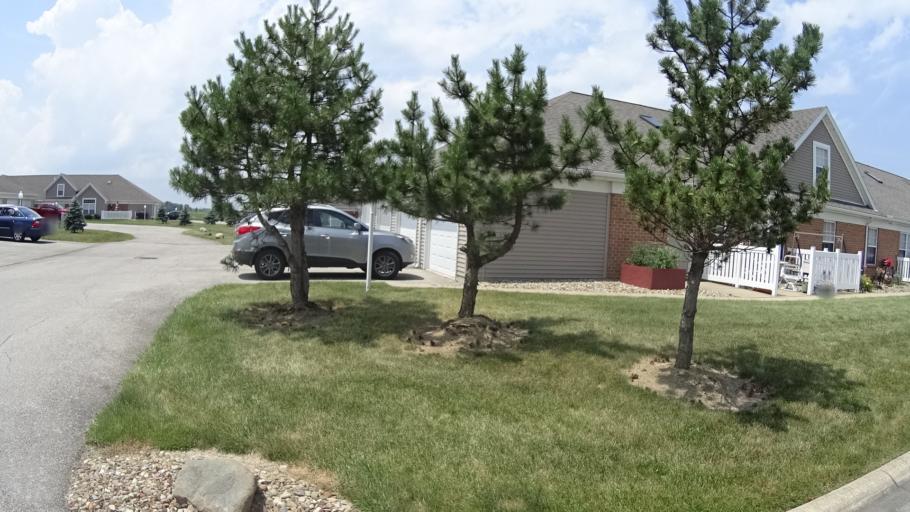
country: US
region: Ohio
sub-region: Lorain County
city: Vermilion
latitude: 41.4072
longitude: -82.3704
